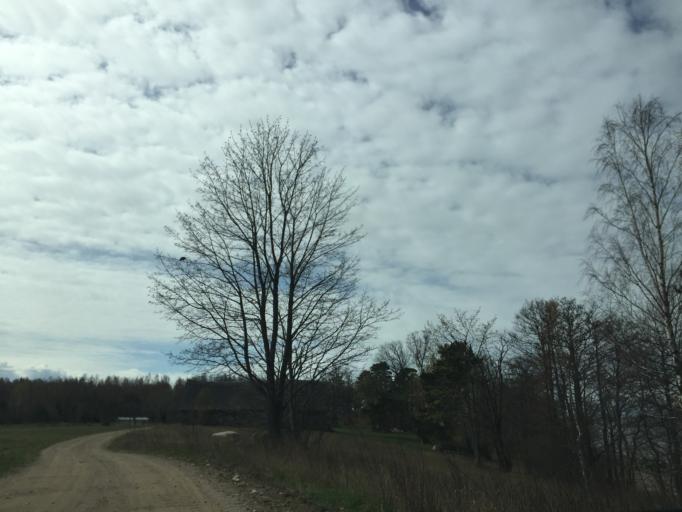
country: LV
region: Salacgrivas
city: Salacgriva
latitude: 57.5903
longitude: 24.3720
